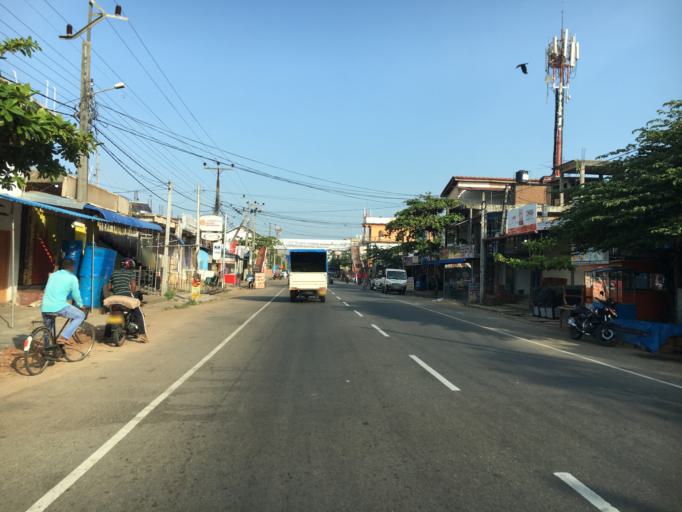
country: LK
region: Eastern Province
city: Eravur Town
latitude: 7.9127
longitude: 81.5262
